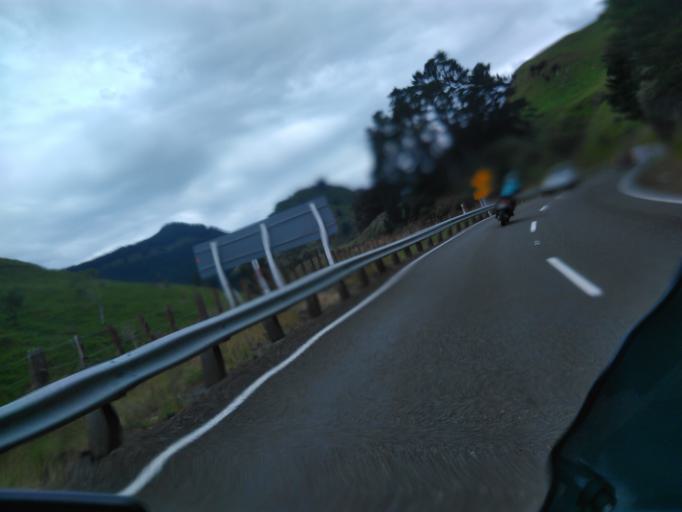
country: NZ
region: Bay of Plenty
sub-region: Opotiki District
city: Opotiki
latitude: -38.3754
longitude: 177.4667
